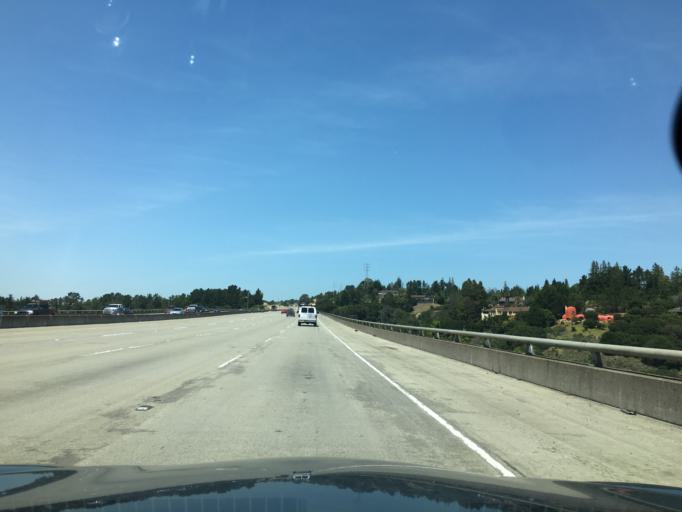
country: US
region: California
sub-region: San Mateo County
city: Highlands-Baywood Park
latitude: 37.5283
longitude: -122.3595
